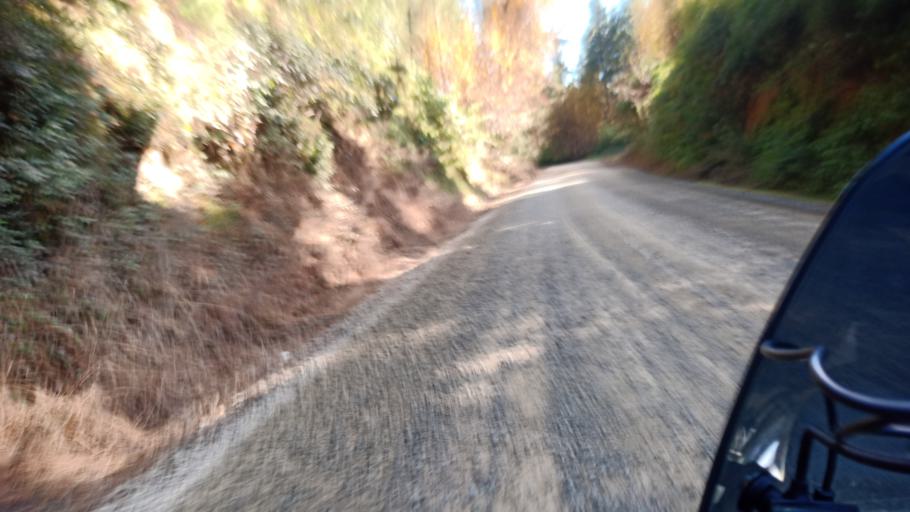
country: NZ
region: Hawke's Bay
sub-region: Wairoa District
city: Wairoa
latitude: -38.9293
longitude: 177.2181
